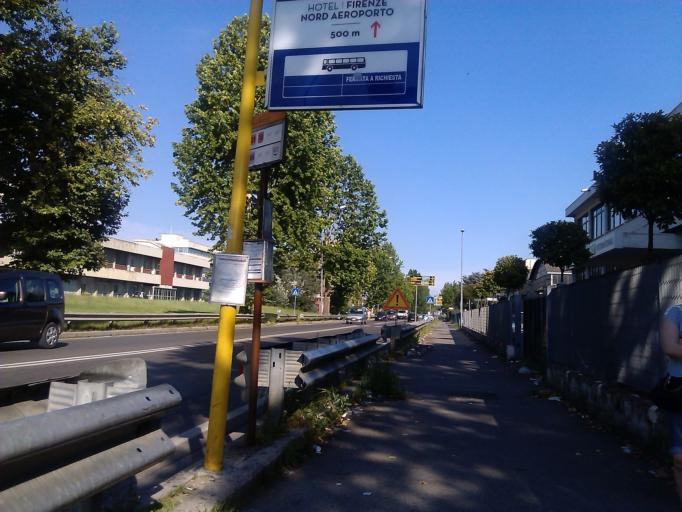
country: IT
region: Tuscany
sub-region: Province of Florence
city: Mantignano-Ugnano
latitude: 43.8094
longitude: 11.1705
